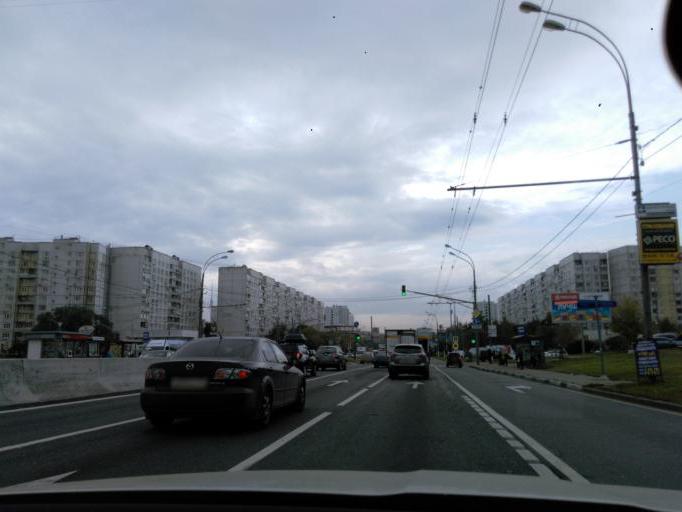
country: RU
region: Moscow
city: Novovladykino
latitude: 55.8576
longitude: 37.5843
